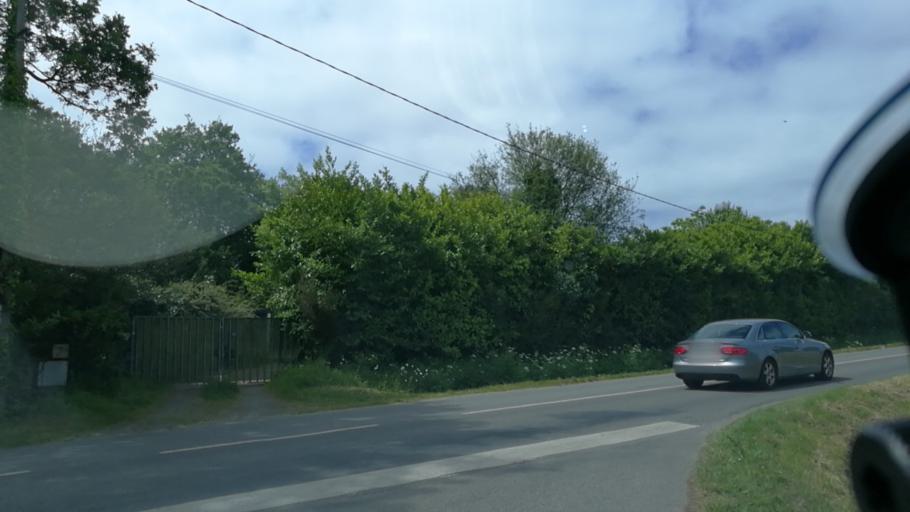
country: FR
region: Pays de la Loire
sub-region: Departement de la Loire-Atlantique
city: Asserac
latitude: 47.4394
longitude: -2.4281
